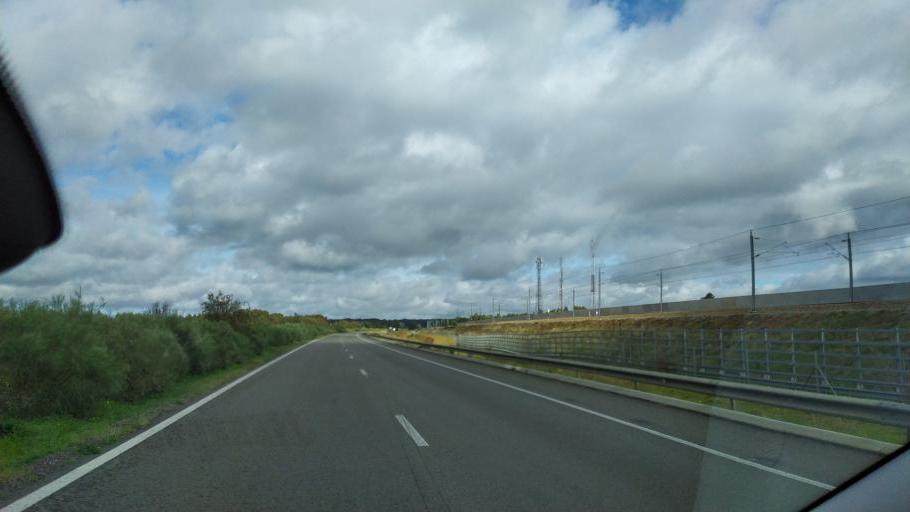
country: MA
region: Gharb-Chrarda-Beni Hssen
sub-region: Kenitra Province
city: Lalla Mimouna
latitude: 34.9003
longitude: -6.2092
